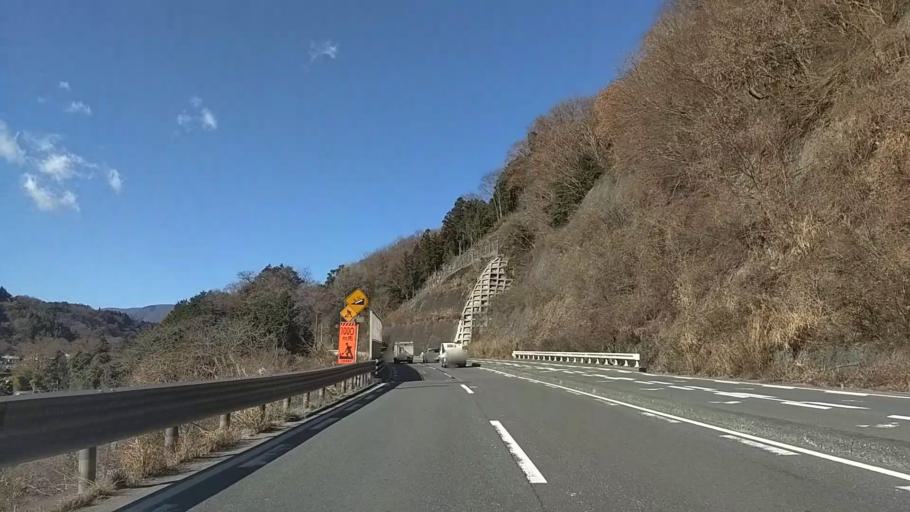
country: JP
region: Shizuoka
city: Gotemba
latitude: 35.3610
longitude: 139.0027
